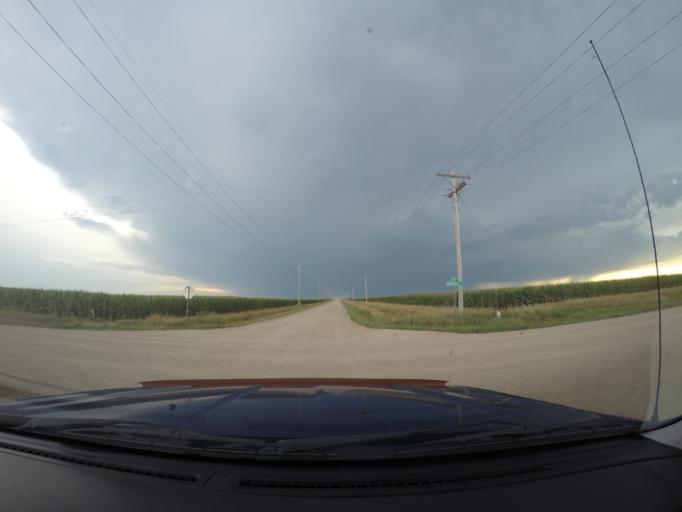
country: US
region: Nebraska
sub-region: Buffalo County
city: Kearney
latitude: 40.8436
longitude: -99.1606
